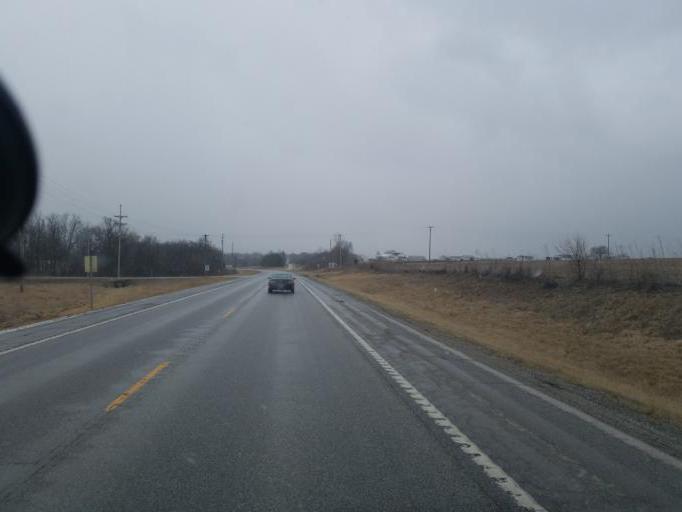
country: US
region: Missouri
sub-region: Schuyler County
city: Lancaster
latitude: 40.3672
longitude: -92.5618
